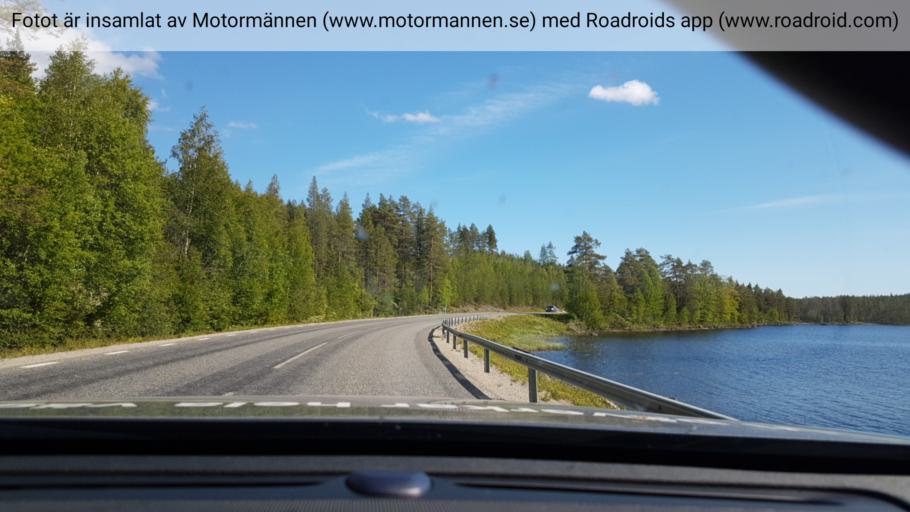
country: SE
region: Vaesterbotten
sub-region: Lycksele Kommun
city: Lycksele
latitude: 64.5900
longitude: 18.6068
